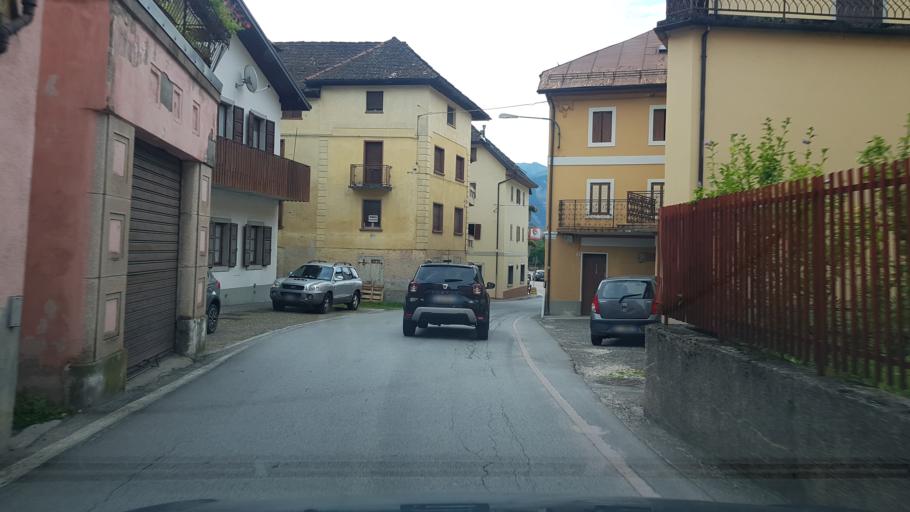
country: IT
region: Friuli Venezia Giulia
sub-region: Provincia di Udine
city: Rigolato
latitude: 46.5532
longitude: 12.8509
